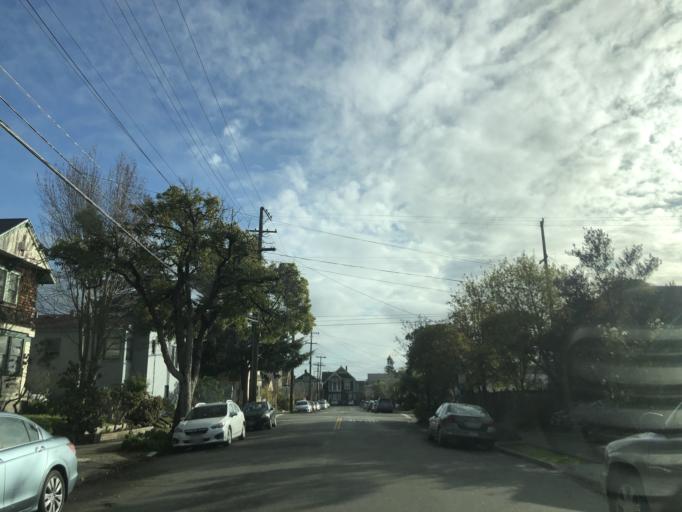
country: US
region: California
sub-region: Alameda County
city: Berkeley
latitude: 37.8532
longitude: -122.2619
